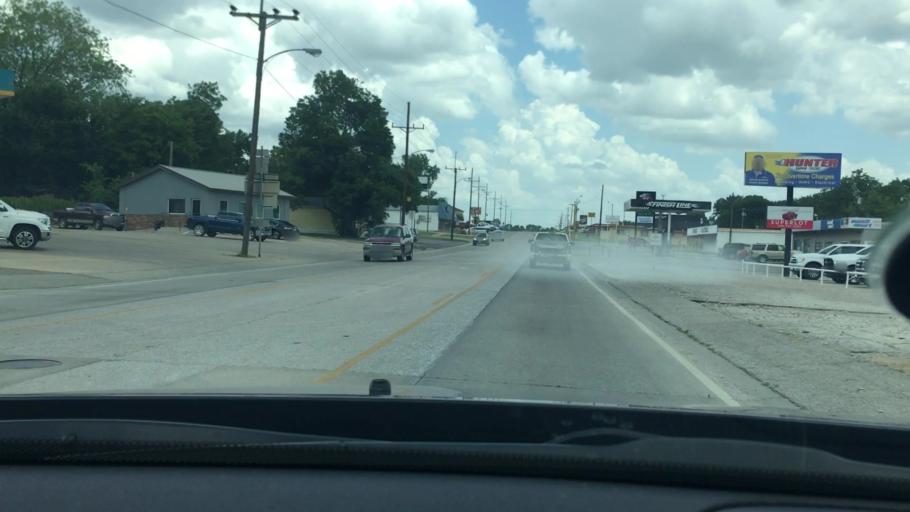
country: US
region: Oklahoma
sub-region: Marshall County
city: Madill
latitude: 34.0940
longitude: -96.7733
